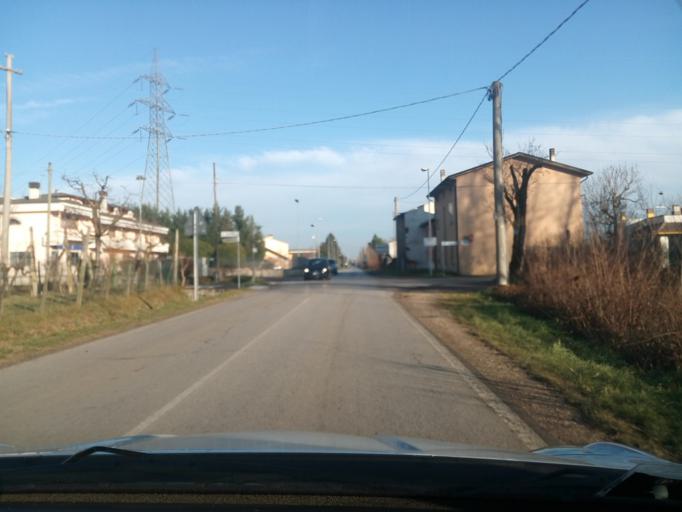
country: IT
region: Veneto
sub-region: Provincia di Vicenza
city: Novoledo
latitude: 45.6402
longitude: 11.5308
